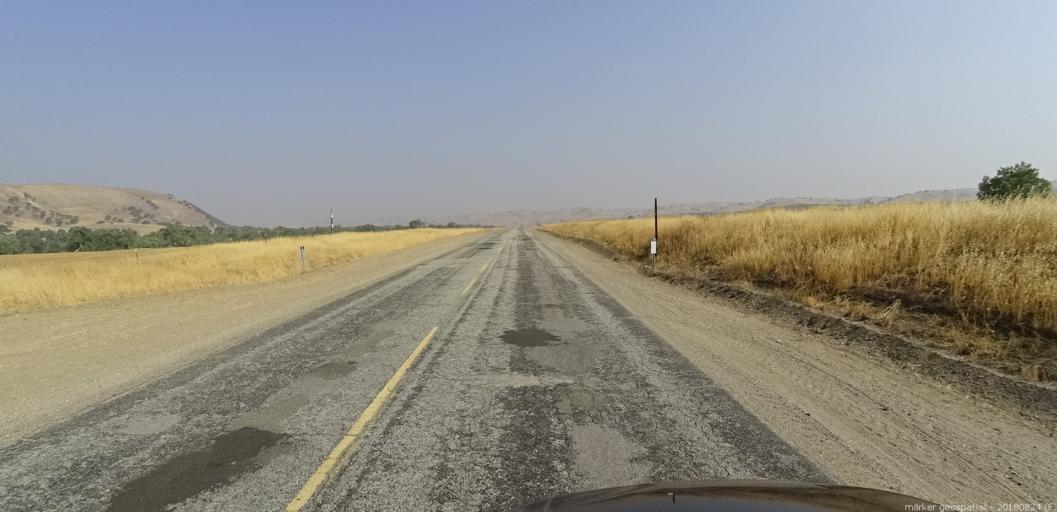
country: US
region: California
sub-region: San Luis Obispo County
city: San Miguel
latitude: 35.8309
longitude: -120.7501
